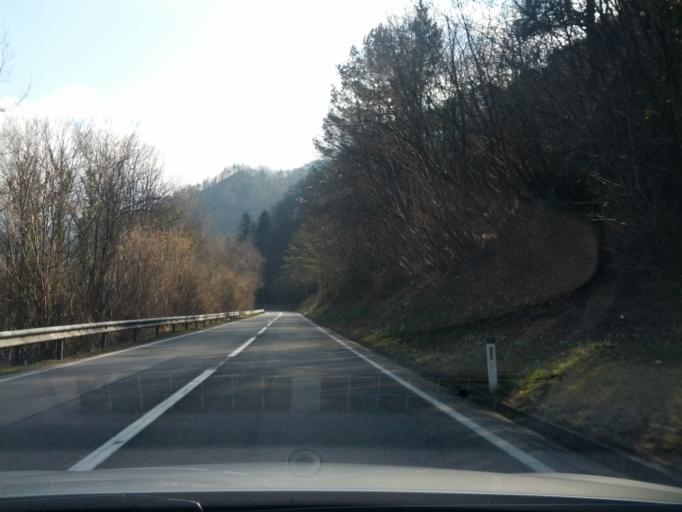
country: SI
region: Zagorje ob Savi
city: Kisovec
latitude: 46.0921
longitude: 14.9152
